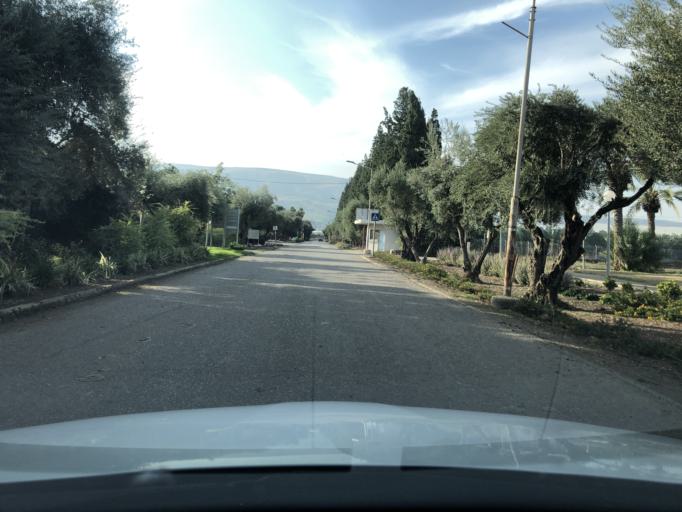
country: IL
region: Northern District
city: Yavne'el
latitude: 32.6583
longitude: 35.5778
